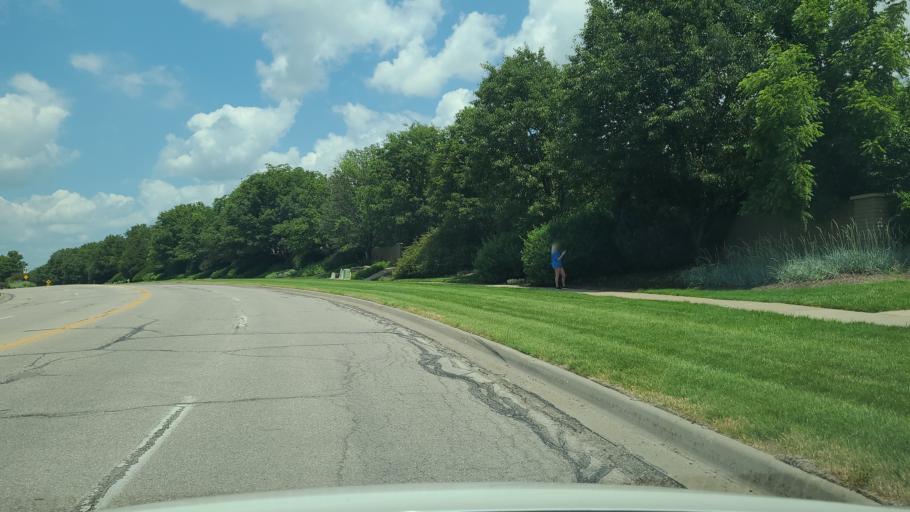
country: US
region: Kansas
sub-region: Douglas County
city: Lawrence
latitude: 38.9791
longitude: -95.3098
